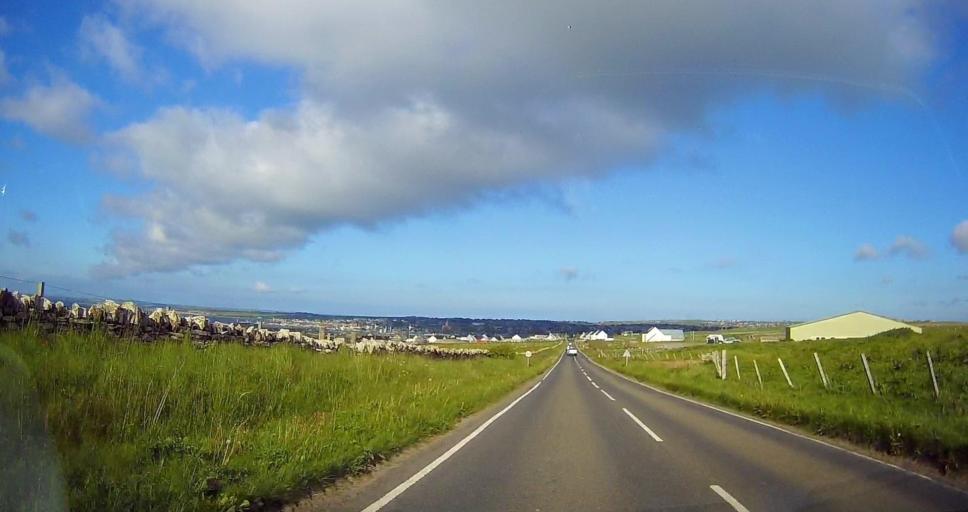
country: GB
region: Scotland
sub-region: Orkney Islands
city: Orkney
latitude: 58.9774
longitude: -2.9967
